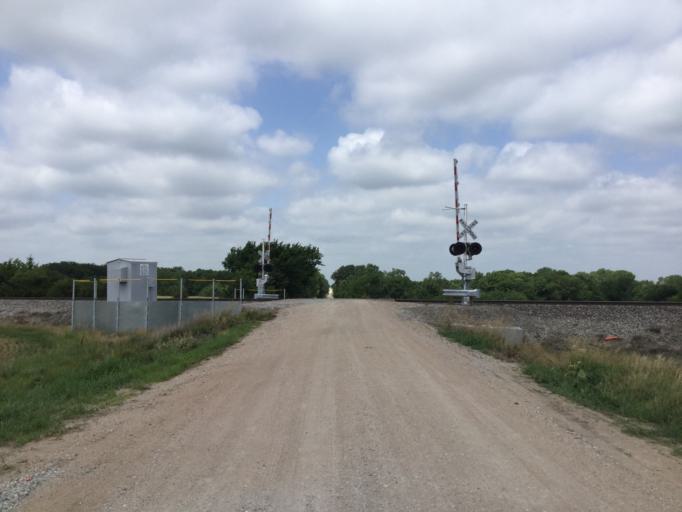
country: US
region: Kansas
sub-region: Sedgwick County
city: Kechi
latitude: 37.9126
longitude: -97.1895
